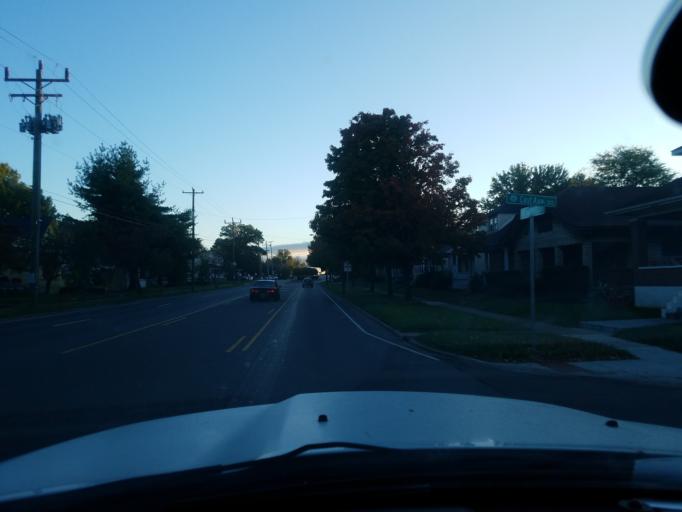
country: US
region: Indiana
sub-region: Floyd County
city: New Albany
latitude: 38.2982
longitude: -85.7969
